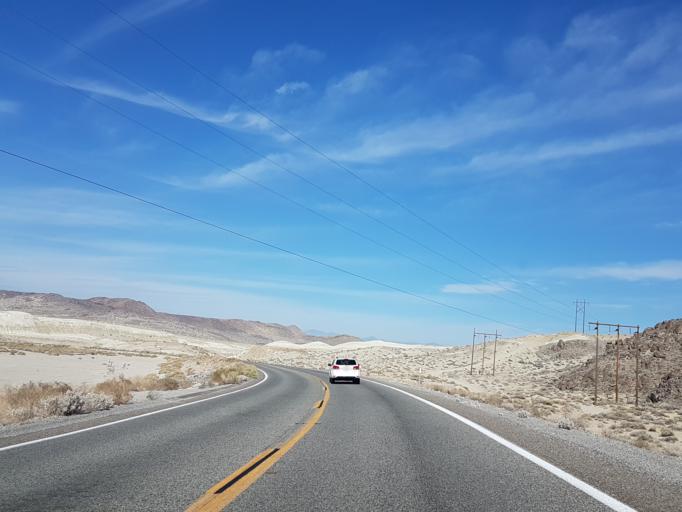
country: US
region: California
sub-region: San Bernardino County
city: Searles Valley
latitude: 35.6636
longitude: -117.4283
